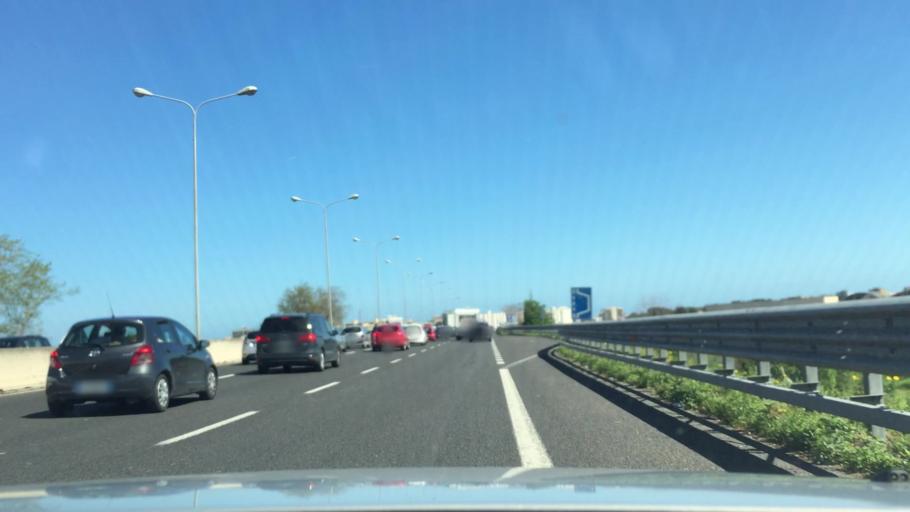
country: IT
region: Apulia
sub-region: Provincia di Bari
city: Triggiano
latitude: 41.0931
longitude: 16.8965
